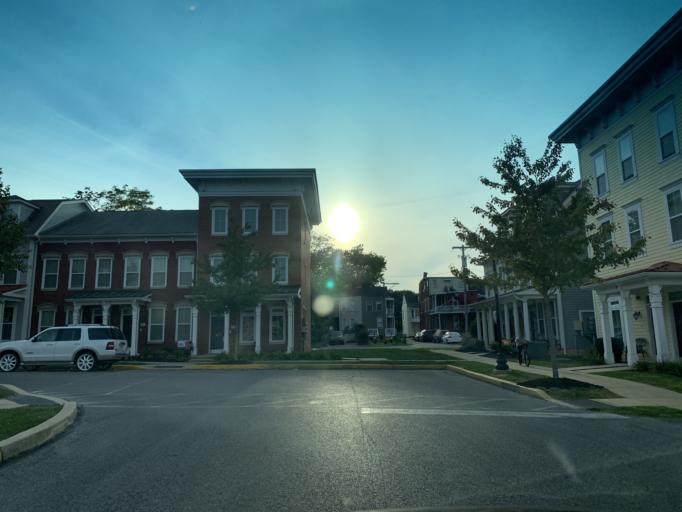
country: US
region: Pennsylvania
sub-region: York County
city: York
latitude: 39.9565
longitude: -76.7341
